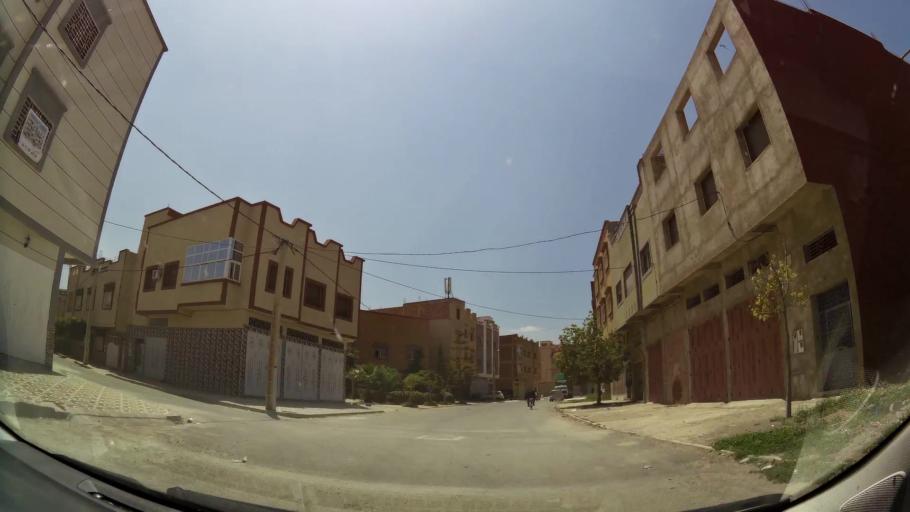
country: MA
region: Oriental
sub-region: Oujda-Angad
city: Oujda
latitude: 34.6938
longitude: -1.8868
